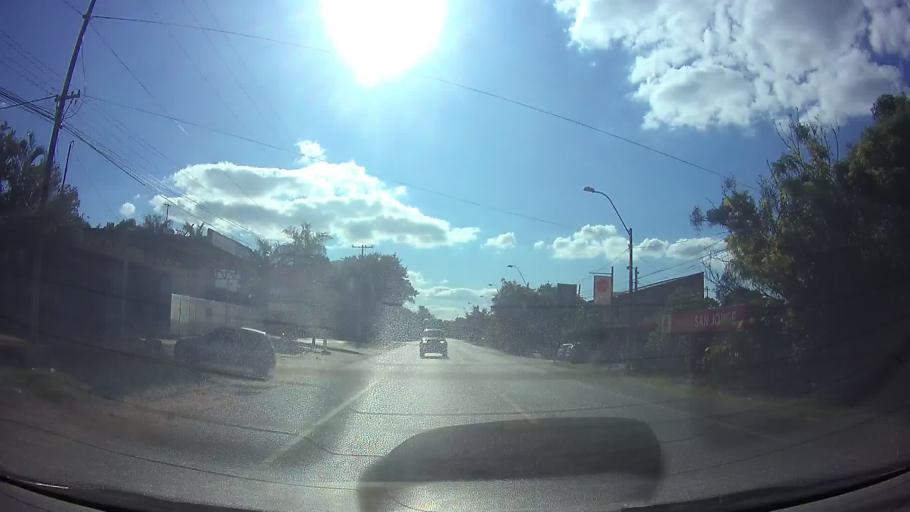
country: PY
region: Cordillera
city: Caacupe
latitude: -25.3895
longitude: -57.1580
